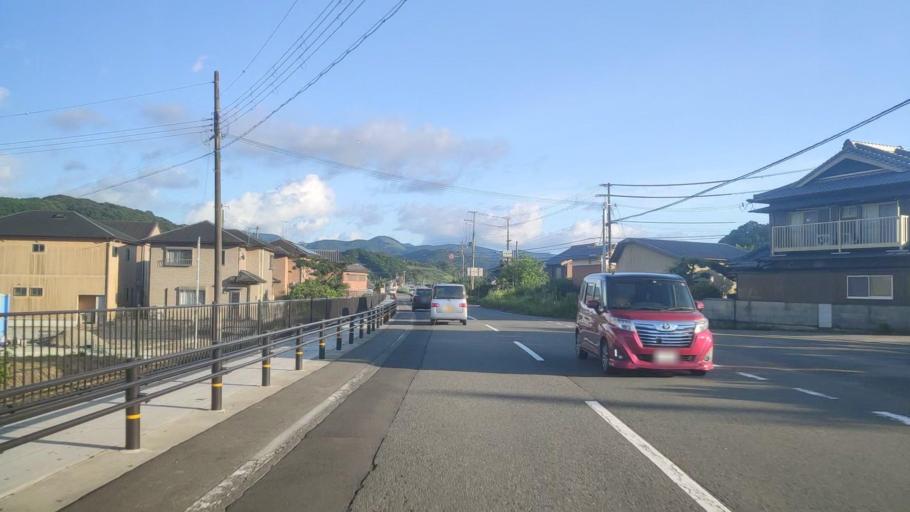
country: JP
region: Wakayama
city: Tanabe
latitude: 33.7202
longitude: 135.4456
